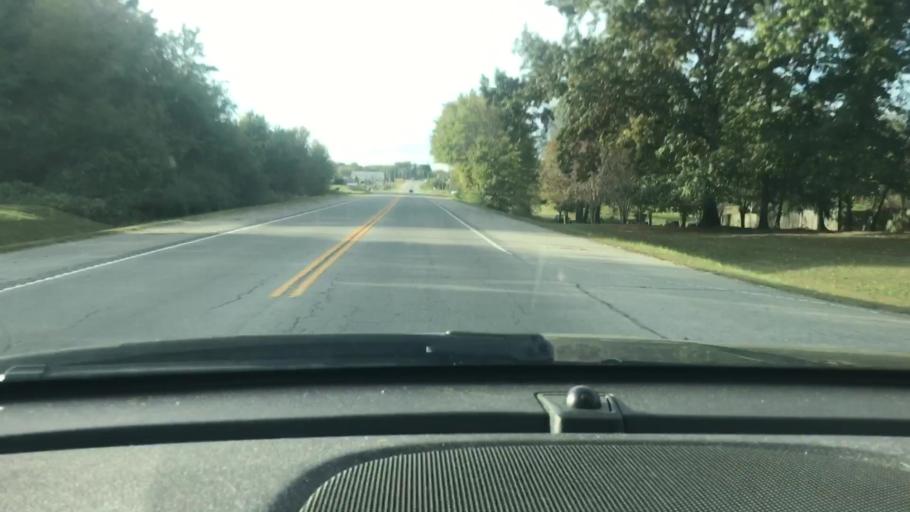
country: US
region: Tennessee
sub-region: Dickson County
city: White Bluff
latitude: 36.1286
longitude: -87.2294
